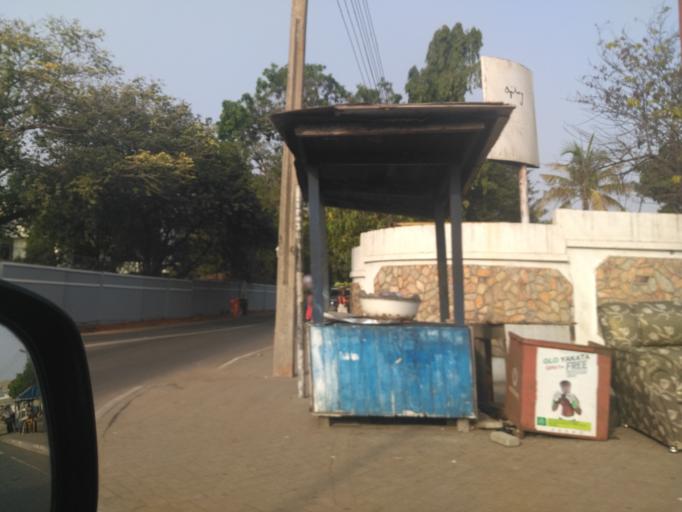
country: GH
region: Greater Accra
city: Accra
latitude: 5.5746
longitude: -0.2008
